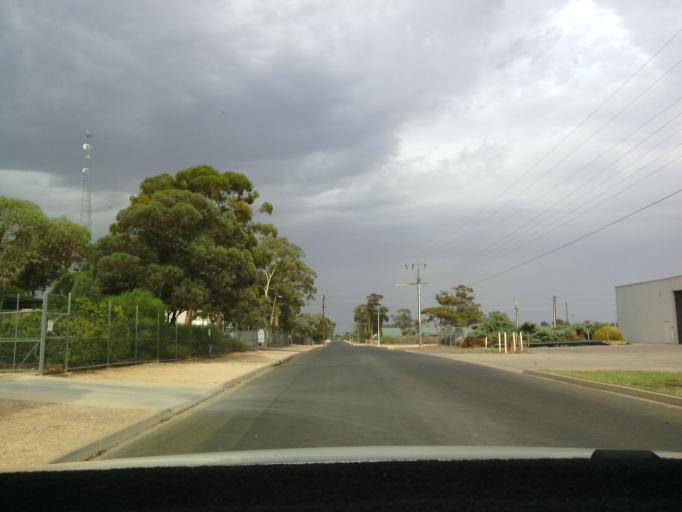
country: AU
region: South Australia
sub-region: Berri and Barmera
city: Berri
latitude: -34.2715
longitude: 140.5993
